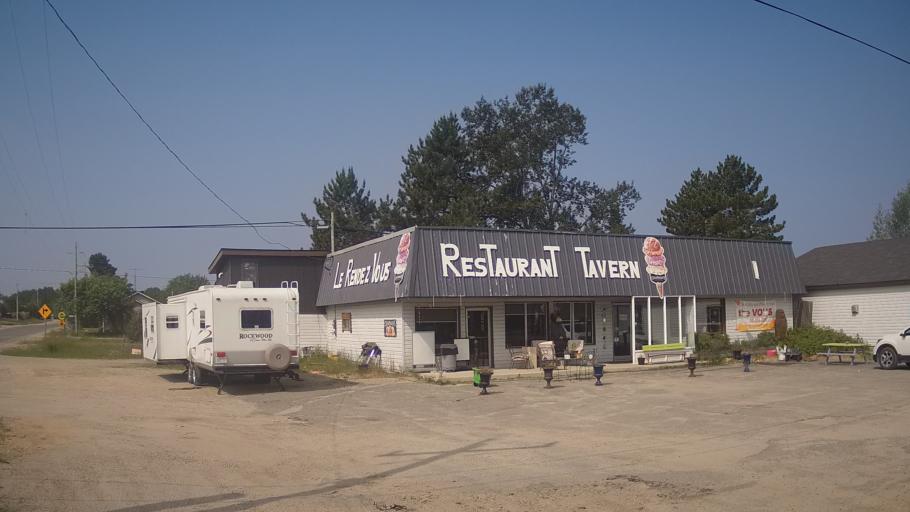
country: CA
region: Ontario
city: Timmins
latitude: 47.6749
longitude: -81.7233
